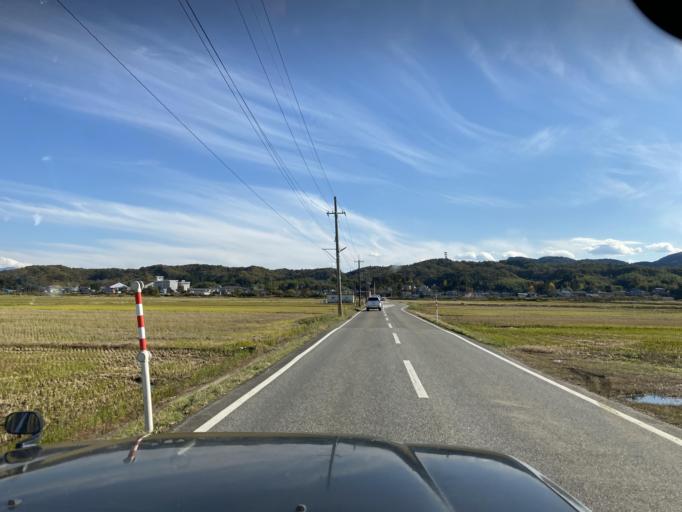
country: JP
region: Niigata
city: Niitsu-honcho
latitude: 37.7557
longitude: 139.0930
